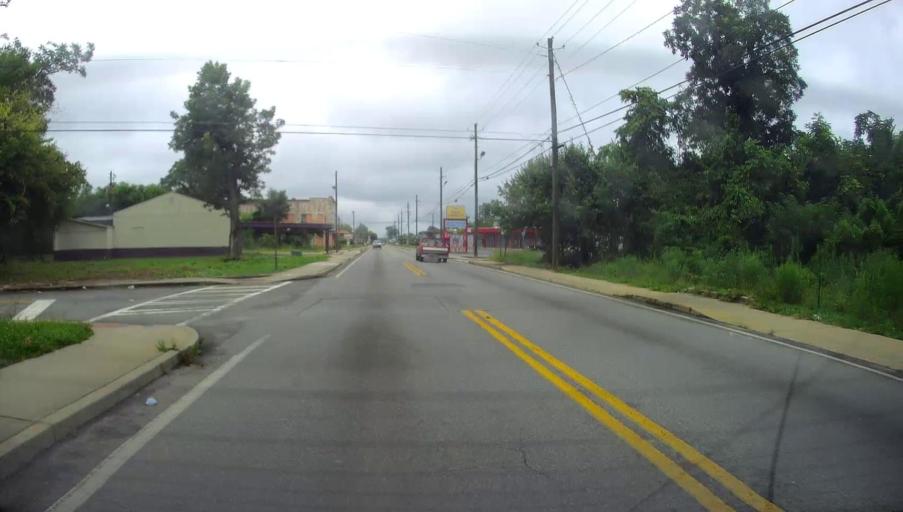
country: US
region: Georgia
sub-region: Bibb County
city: Macon
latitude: 32.8087
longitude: -83.6473
